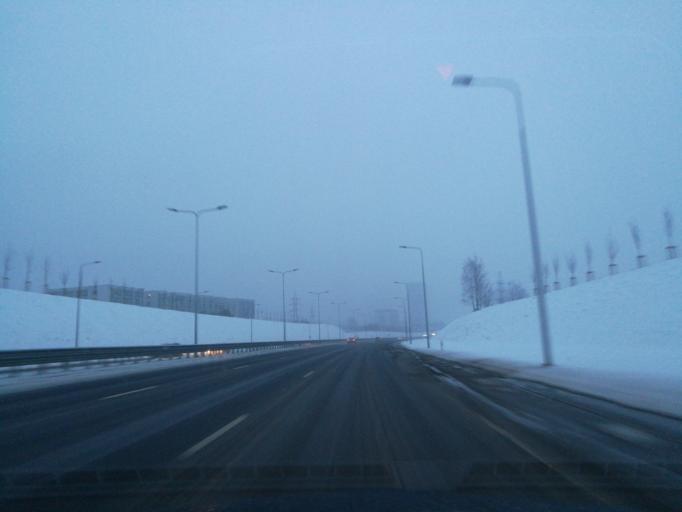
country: LT
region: Vilnius County
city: Justiniskes
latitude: 54.7102
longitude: 25.2089
